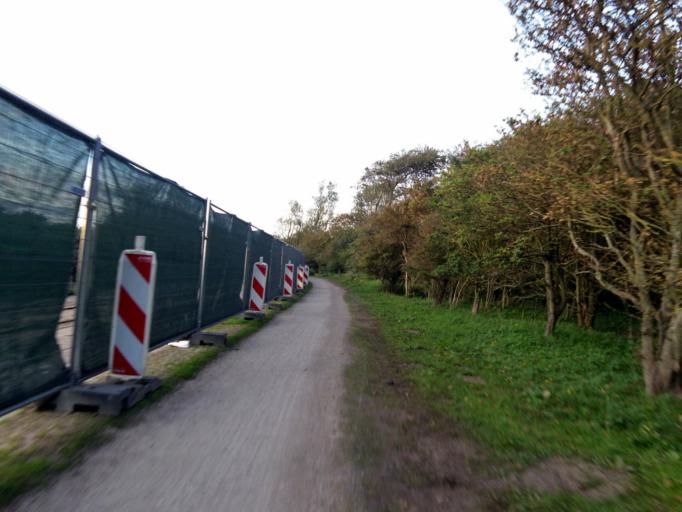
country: NL
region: South Holland
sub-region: Gemeente Den Haag
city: Scheveningen
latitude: 52.1191
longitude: 4.3059
